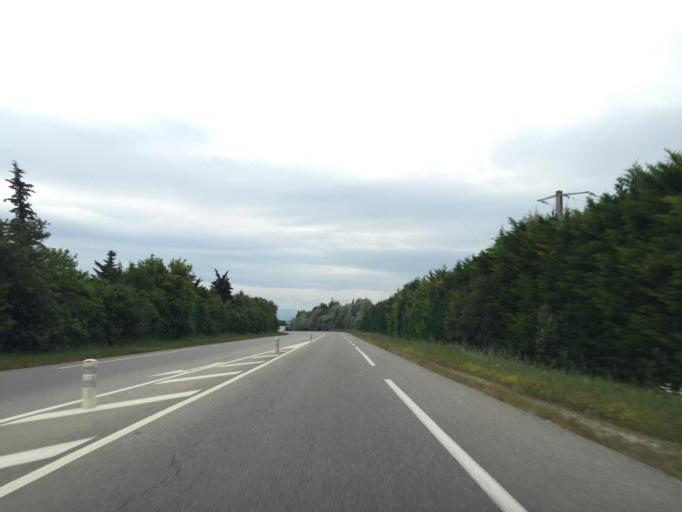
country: FR
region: Rhone-Alpes
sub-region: Departement de la Drome
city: Chabeuil
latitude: 44.9066
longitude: 5.0137
